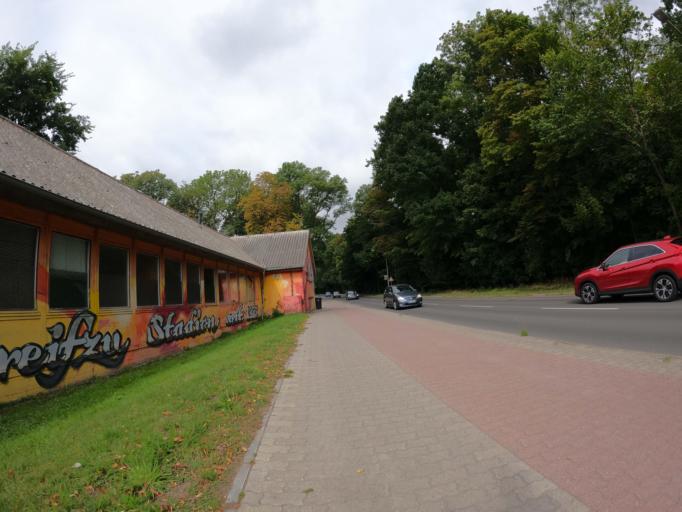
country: DE
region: Mecklenburg-Vorpommern
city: Stralsund
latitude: 54.3150
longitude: 13.0538
